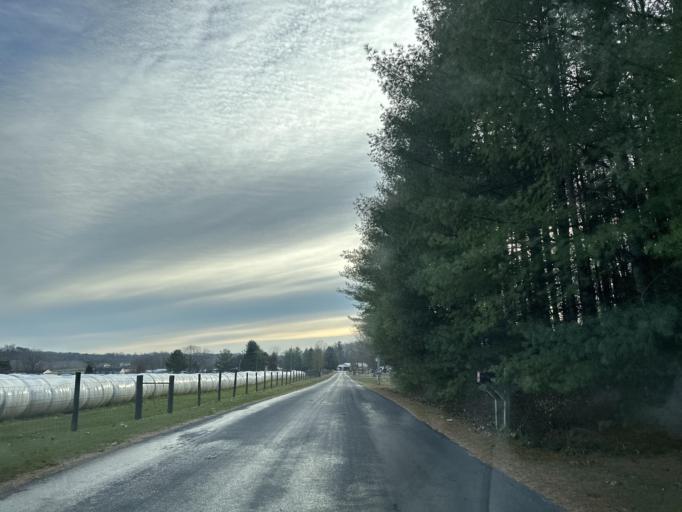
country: US
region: Virginia
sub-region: City of Staunton
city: Staunton
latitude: 38.2457
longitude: -79.1964
